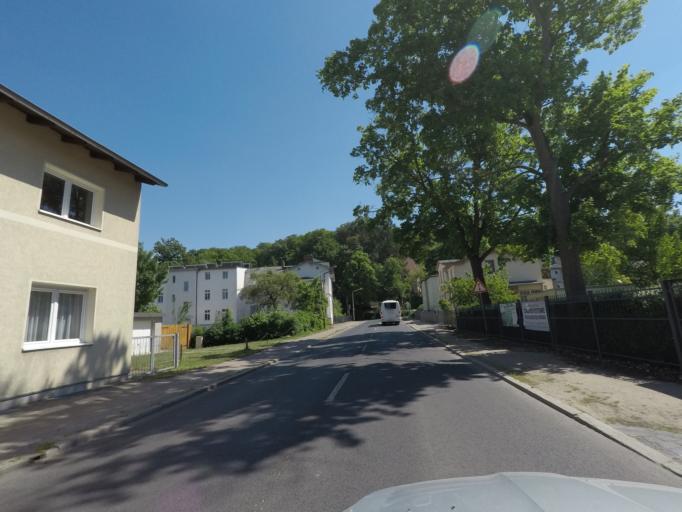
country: DE
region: Brandenburg
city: Eberswalde
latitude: 52.8283
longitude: 13.8085
